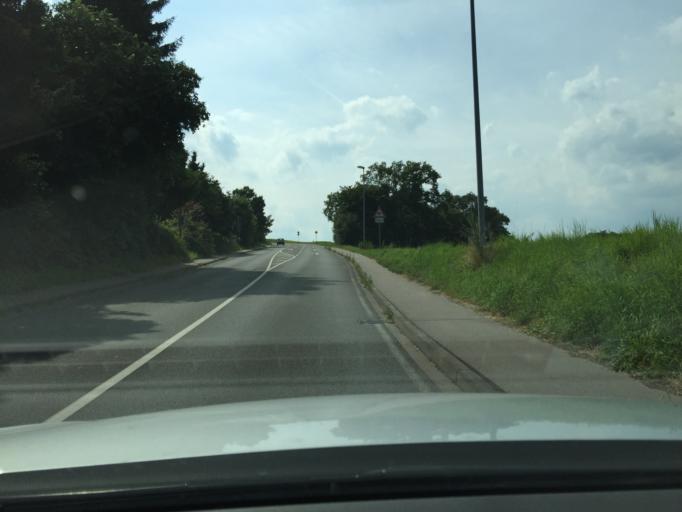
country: DE
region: North Rhine-Westphalia
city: Hattingen
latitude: 51.3673
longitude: 7.1163
